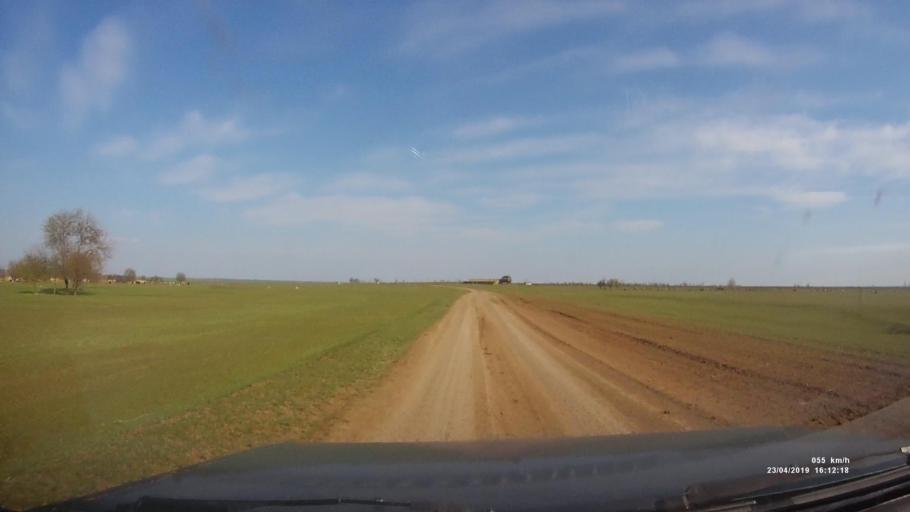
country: RU
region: Kalmykiya
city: Priyutnoye
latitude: 46.4671
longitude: 43.1250
